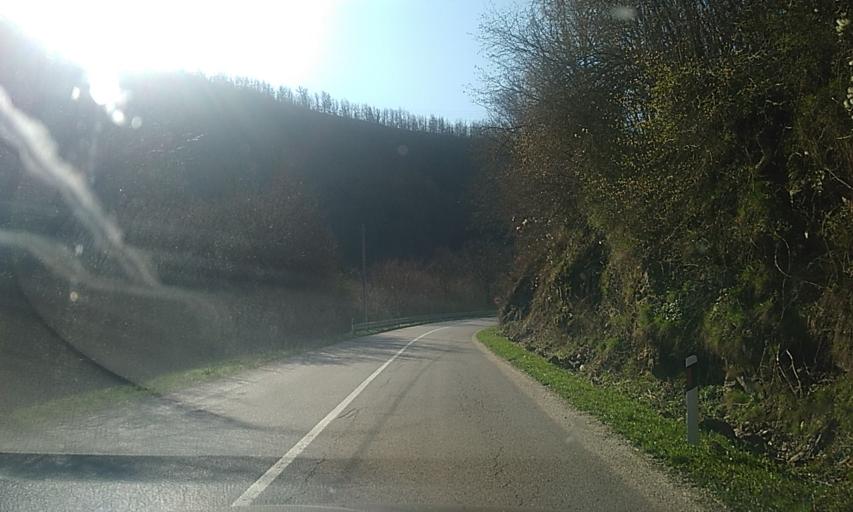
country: RS
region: Central Serbia
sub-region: Pcinjski Okrug
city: Bosilegrad
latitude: 42.4448
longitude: 22.5056
